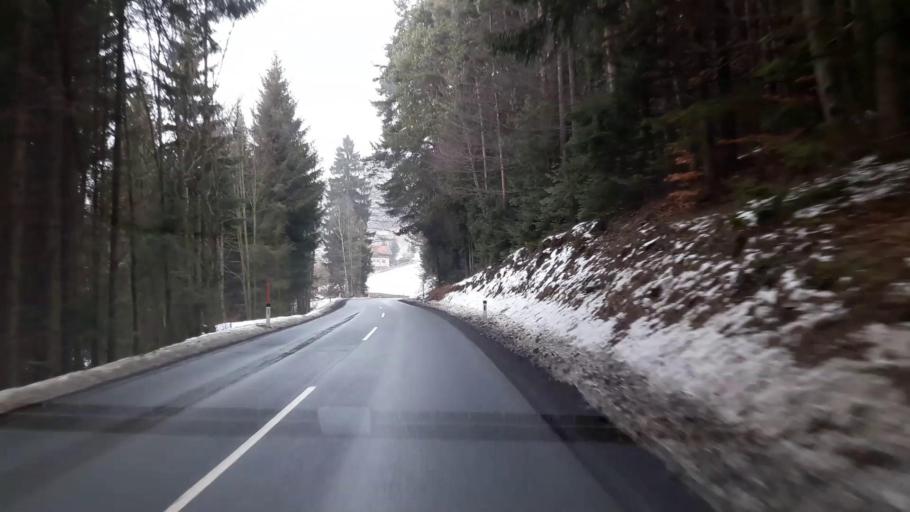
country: AT
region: Lower Austria
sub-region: Politischer Bezirk Neunkirchen
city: Feistritz am Wechsel
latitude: 47.5678
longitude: 16.0436
